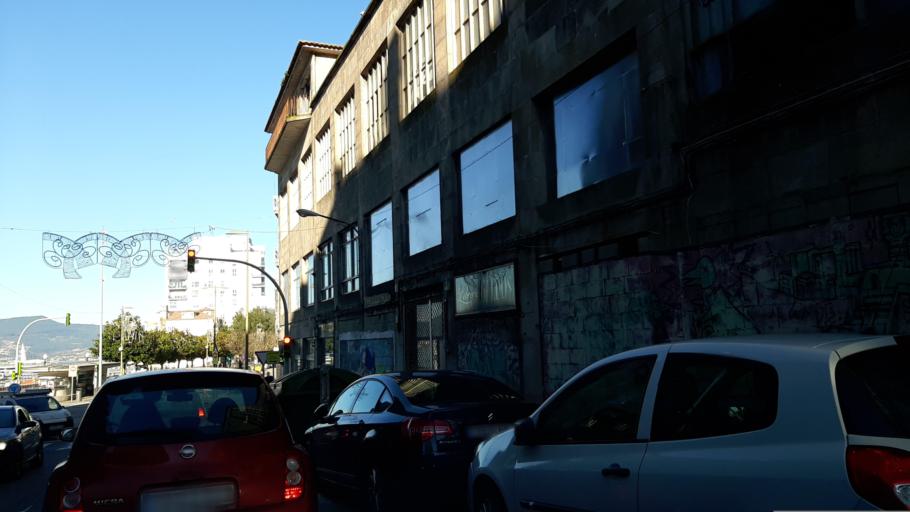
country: ES
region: Galicia
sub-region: Provincia de Pontevedra
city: Vigo
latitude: 42.2353
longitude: -8.7286
